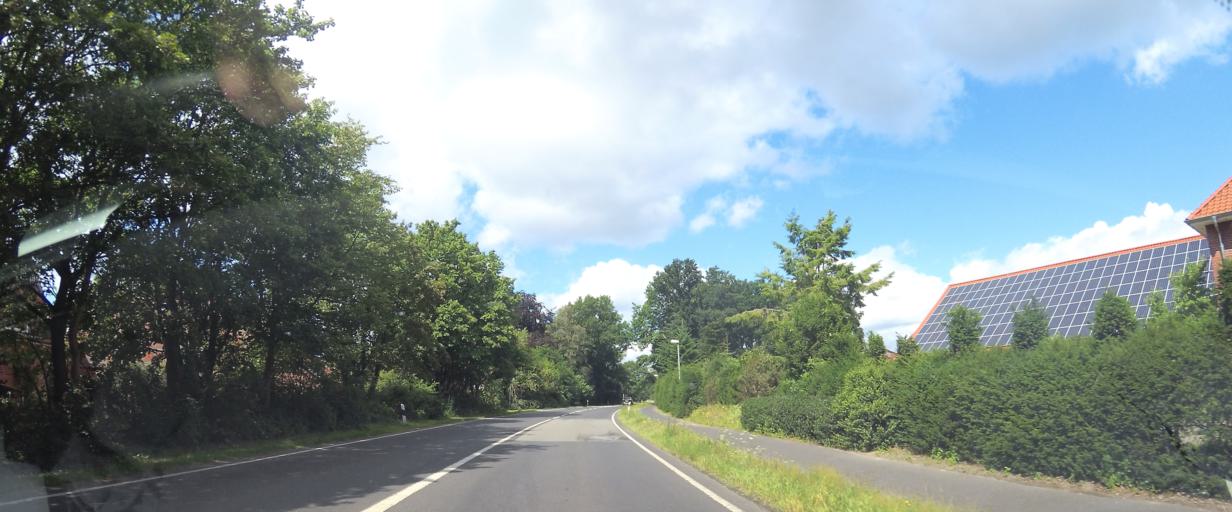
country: DE
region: Lower Saxony
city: Haren
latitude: 52.7876
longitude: 7.2767
